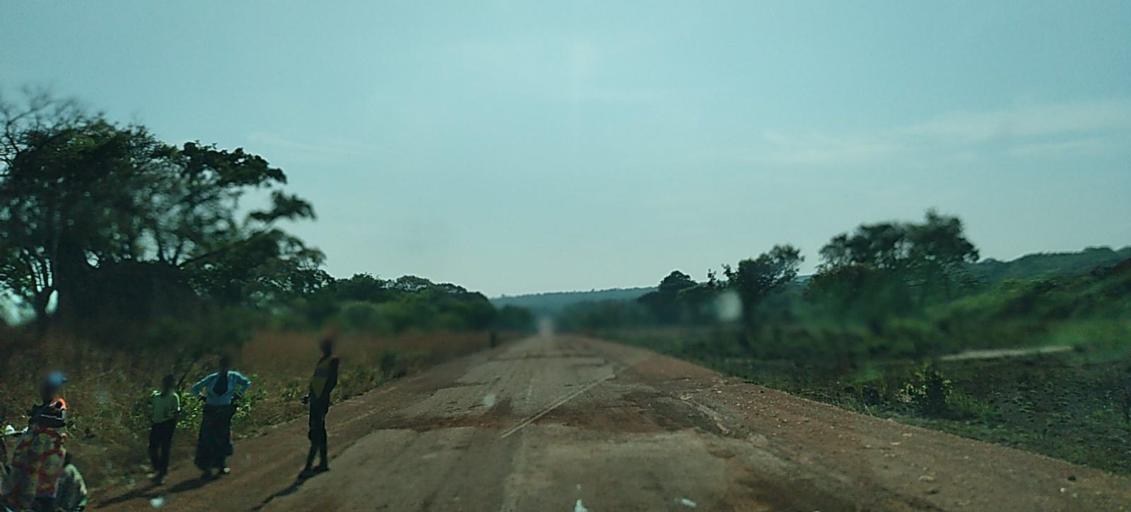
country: ZM
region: North-Western
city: Mwinilunga
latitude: -11.7860
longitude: 25.0336
